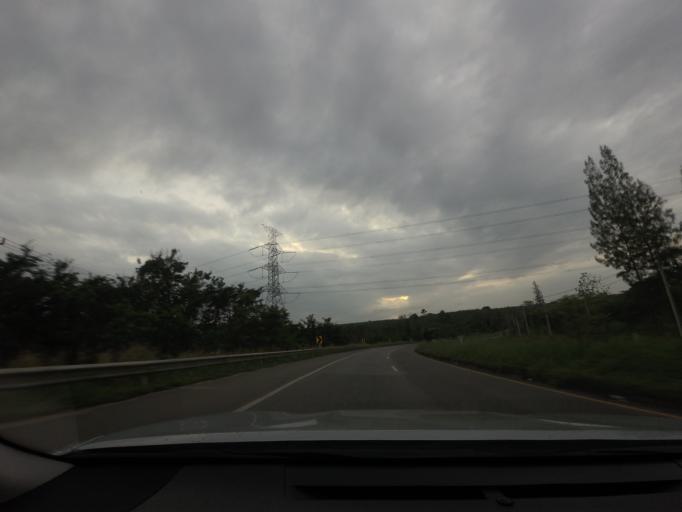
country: TH
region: Surat Thani
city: Phunphin
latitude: 9.0364
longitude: 99.1040
